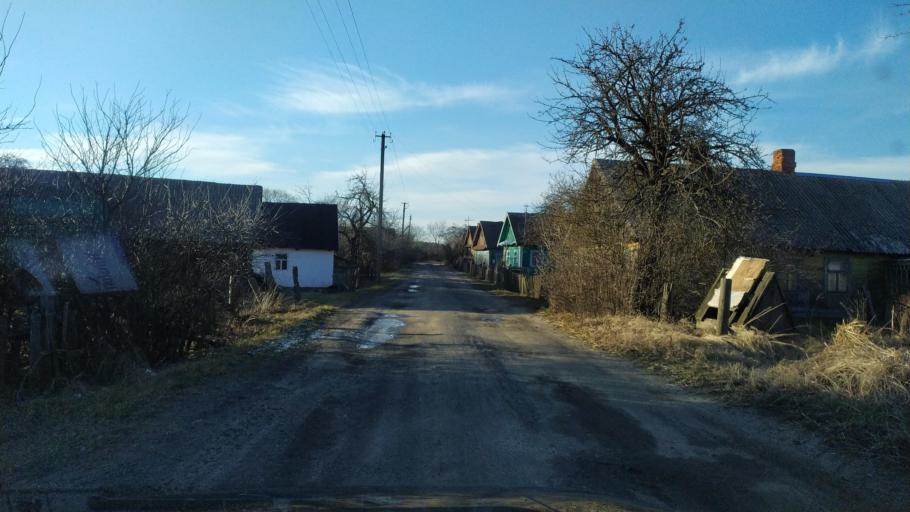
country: BY
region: Brest
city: Pruzhany
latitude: 52.5512
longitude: 24.2929
